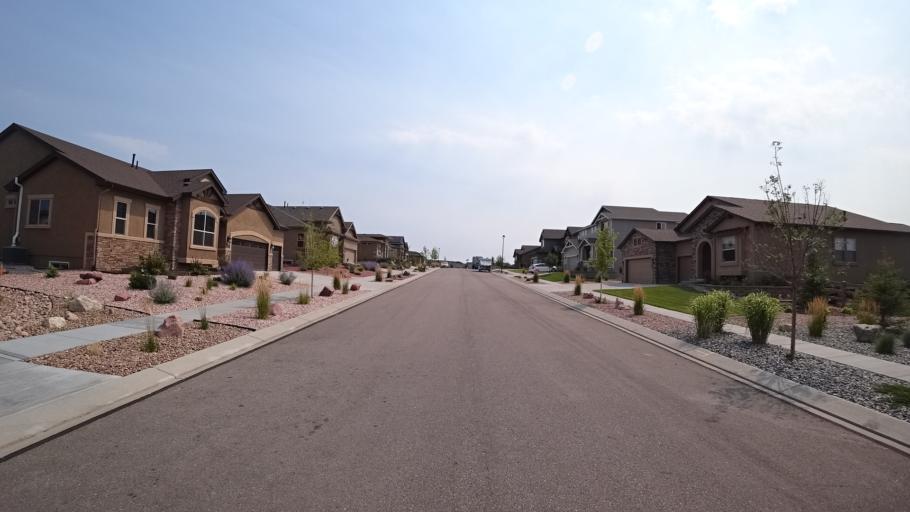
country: US
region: Colorado
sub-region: El Paso County
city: Black Forest
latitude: 38.9700
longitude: -104.7214
